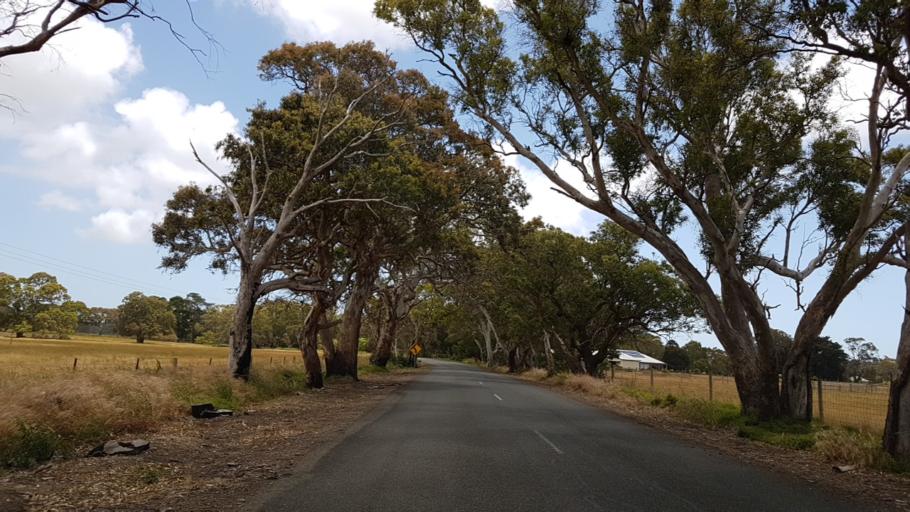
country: AU
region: South Australia
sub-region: Onkaparinga
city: Aldinga
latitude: -35.3774
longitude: 138.4889
